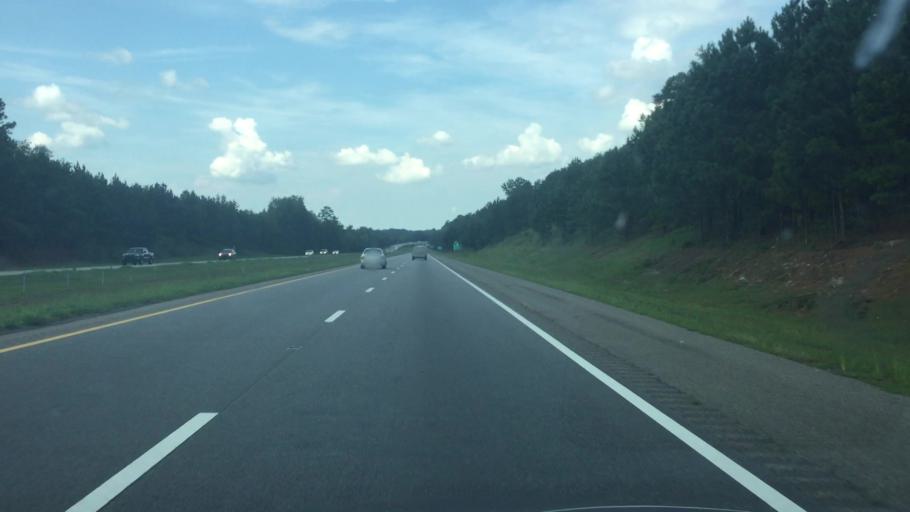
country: US
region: North Carolina
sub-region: Richmond County
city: Hamlet
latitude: 34.8536
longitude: -79.7185
